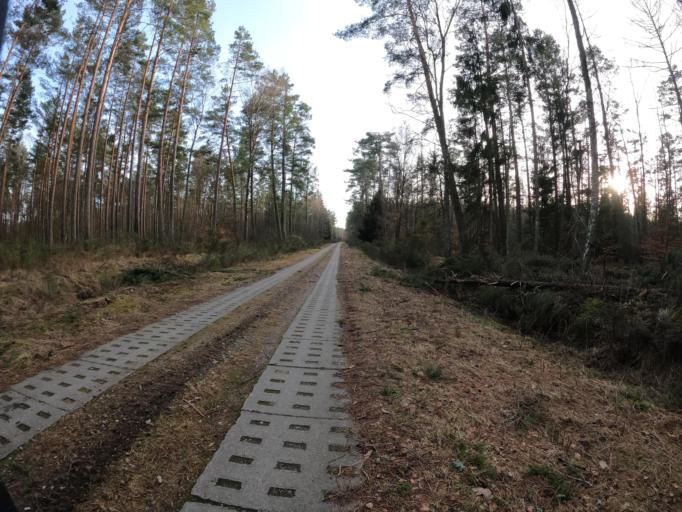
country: PL
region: West Pomeranian Voivodeship
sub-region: Powiat koszalinski
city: Polanow
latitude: 54.1323
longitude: 16.6636
